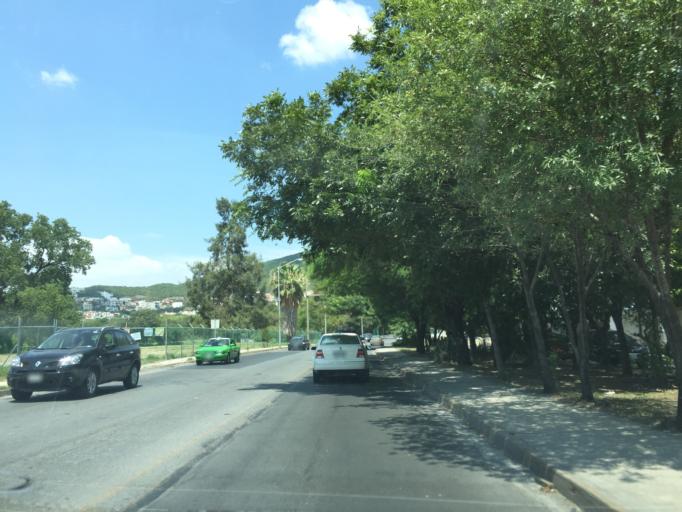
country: MX
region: Nuevo Leon
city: Guadalupe
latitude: 25.6478
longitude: -100.2716
